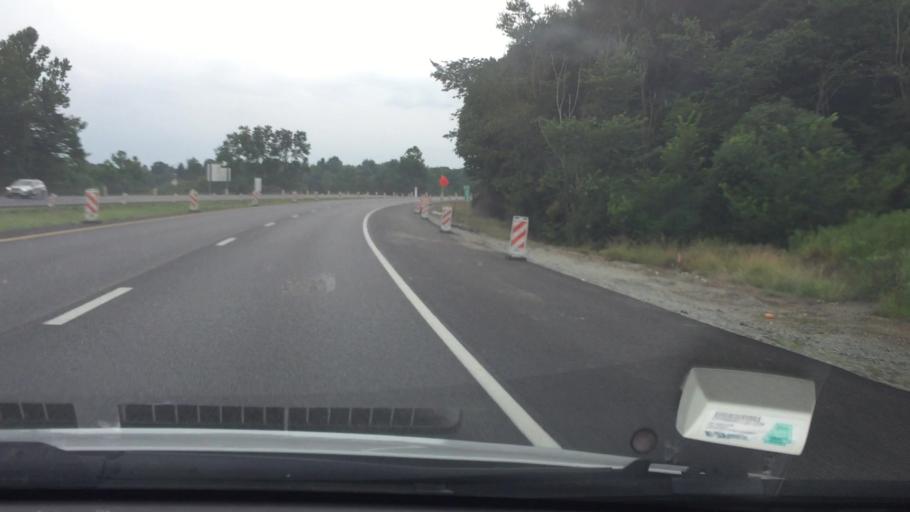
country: US
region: Pennsylvania
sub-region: Allegheny County
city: Brackenridge
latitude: 40.6408
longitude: -79.7209
